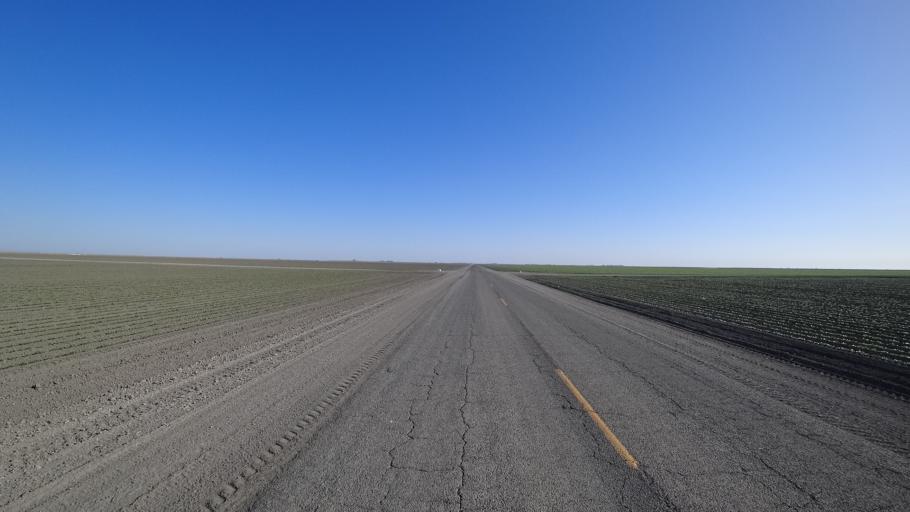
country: US
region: California
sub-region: Kings County
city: Stratford
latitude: 36.1007
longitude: -119.7979
